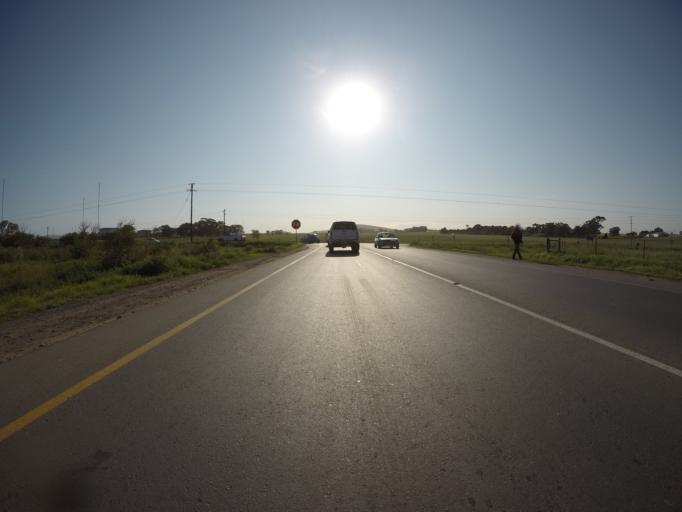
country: ZA
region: Western Cape
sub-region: City of Cape Town
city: Kraaifontein
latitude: -33.7846
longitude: 18.7041
